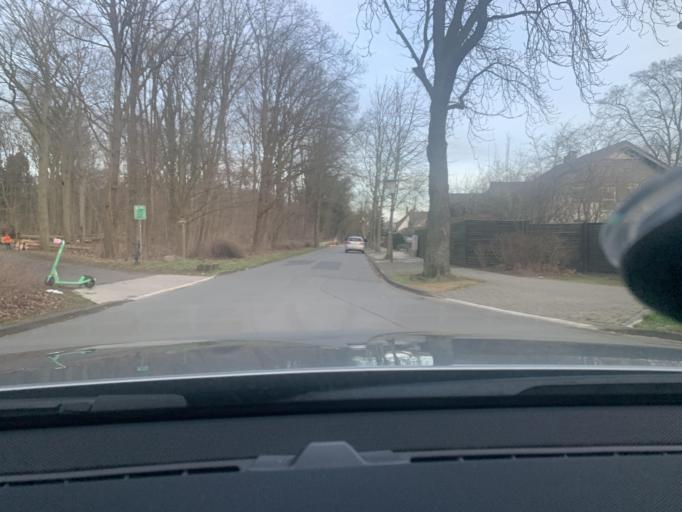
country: DE
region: Lower Saxony
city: Peine
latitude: 52.3325
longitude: 10.2244
